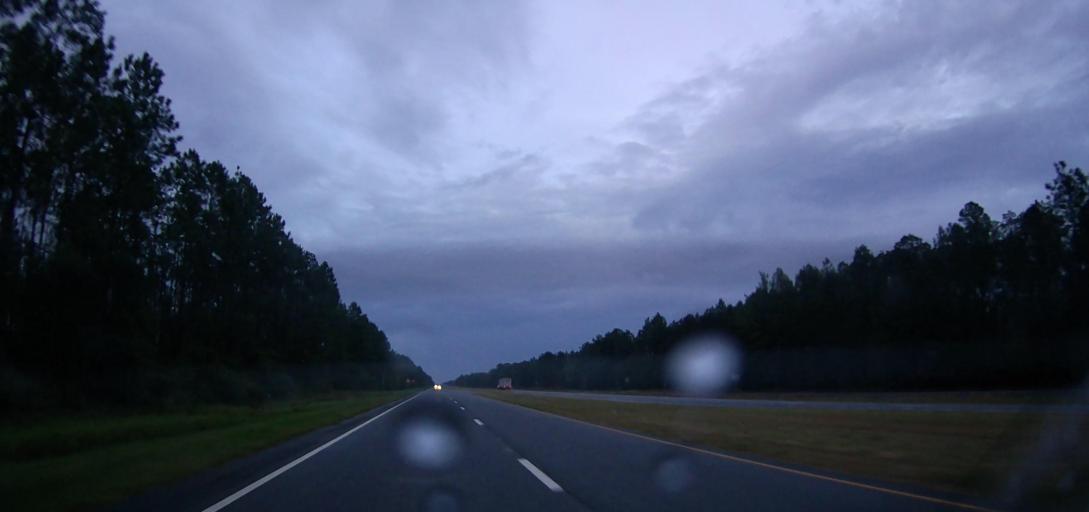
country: US
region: Georgia
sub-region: Lowndes County
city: Valdosta
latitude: 30.8774
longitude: -83.1575
